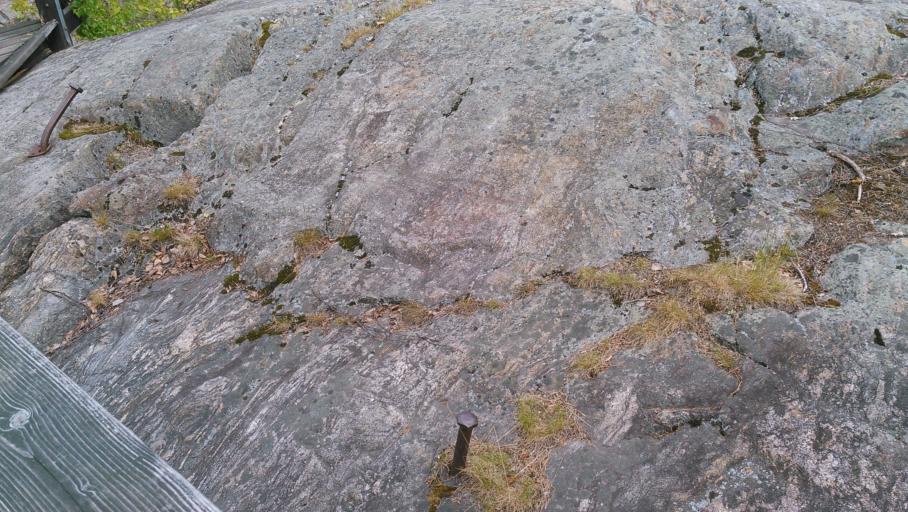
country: SE
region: Vaesterbotten
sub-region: Umea Kommun
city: Roback
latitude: 63.8791
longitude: 20.0249
